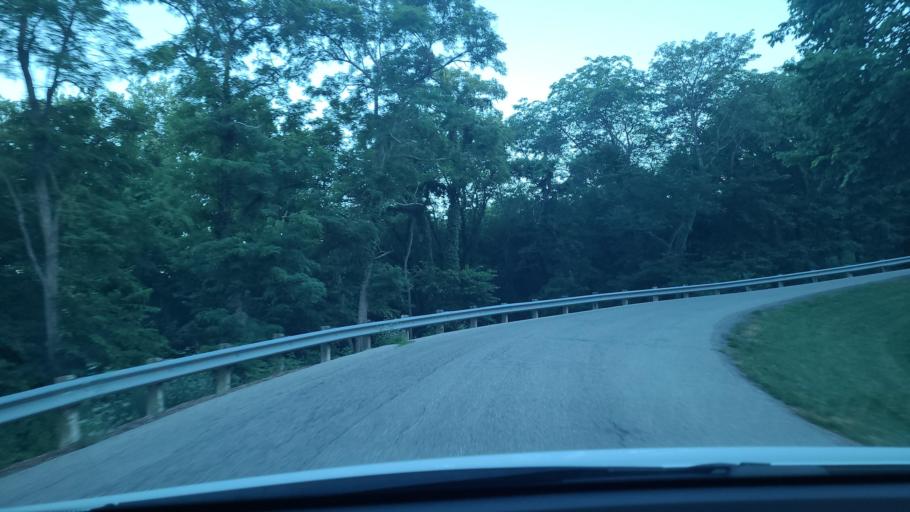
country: US
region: Kansas
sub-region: Douglas County
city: Lawrence
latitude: 38.8829
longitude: -95.2467
